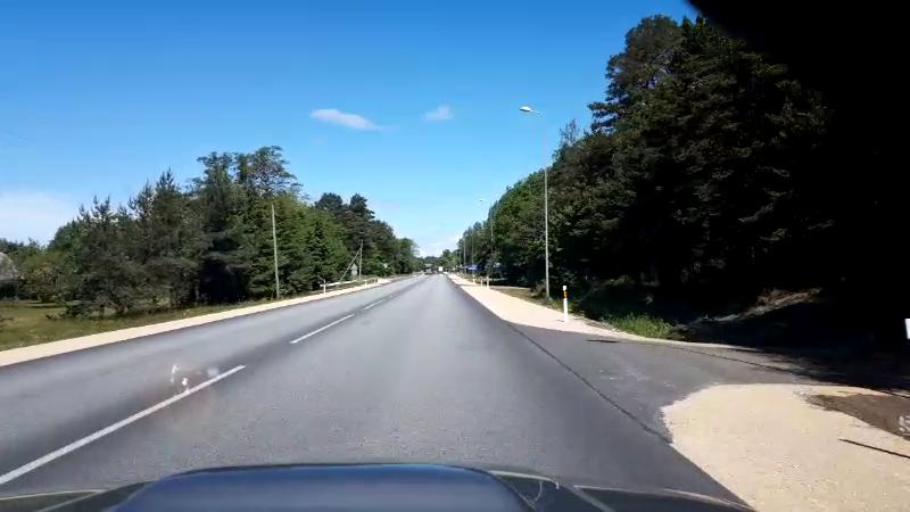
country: LV
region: Salacgrivas
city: Salacgriva
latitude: 57.7843
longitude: 24.3548
